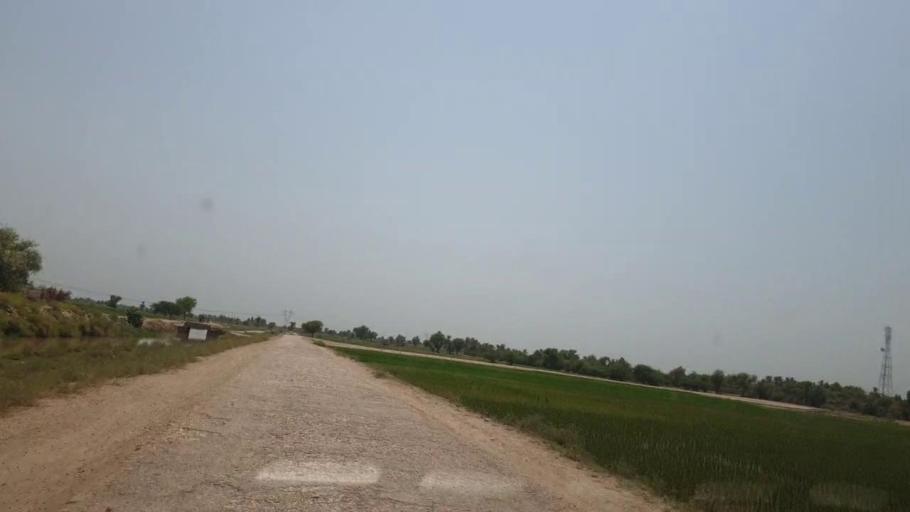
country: PK
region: Sindh
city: Lakhi
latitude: 27.8625
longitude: 68.6059
